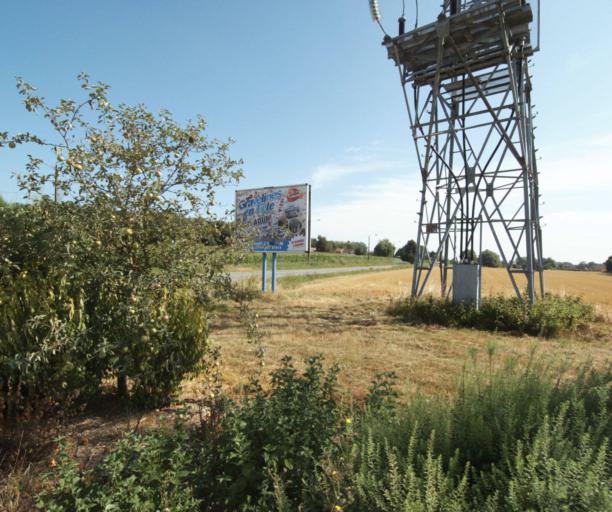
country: FR
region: Nord-Pas-de-Calais
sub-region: Departement du Nord
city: Bousbecque
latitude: 50.7711
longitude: 3.1068
